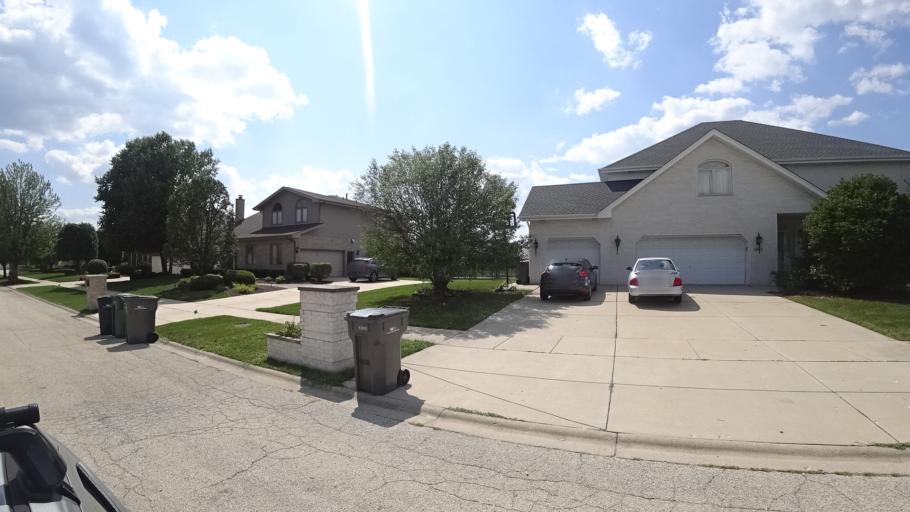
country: US
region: Illinois
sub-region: Cook County
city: Palos Park
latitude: 41.6340
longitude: -87.8142
